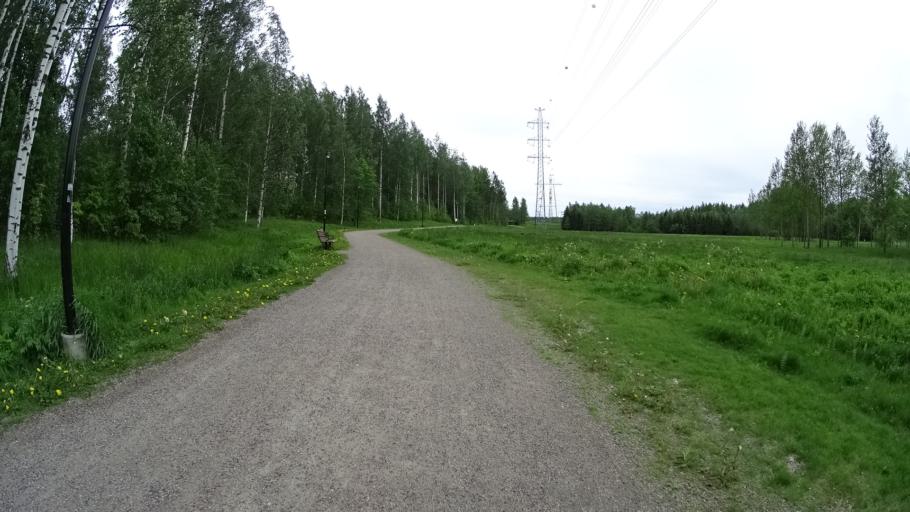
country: FI
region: Uusimaa
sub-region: Helsinki
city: Vantaa
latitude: 60.2828
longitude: 25.0580
